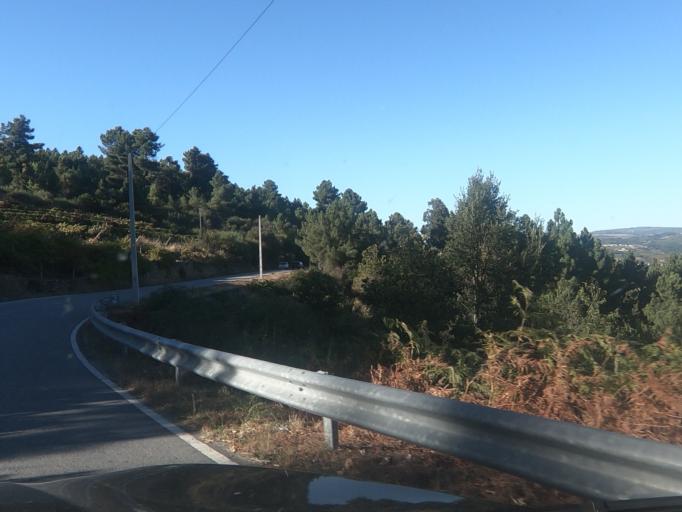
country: PT
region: Vila Real
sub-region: Sabrosa
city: Sabrosa
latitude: 41.2748
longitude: -7.5683
